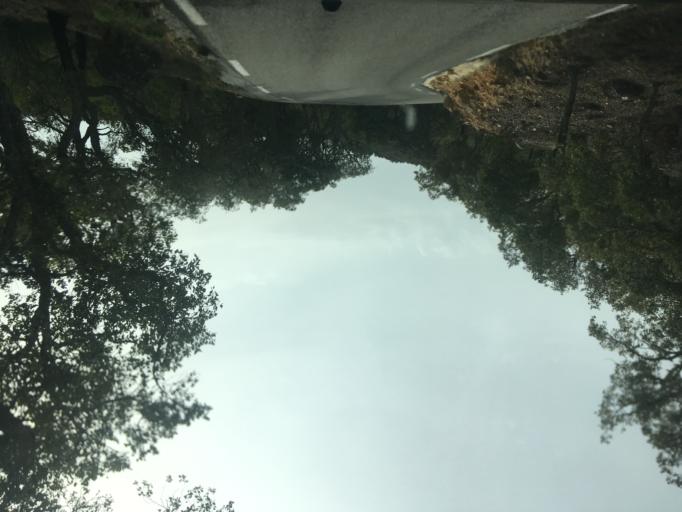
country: FR
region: Provence-Alpes-Cote d'Azur
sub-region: Departement du Var
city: Bagnols-en-Foret
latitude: 43.5165
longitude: 6.6347
